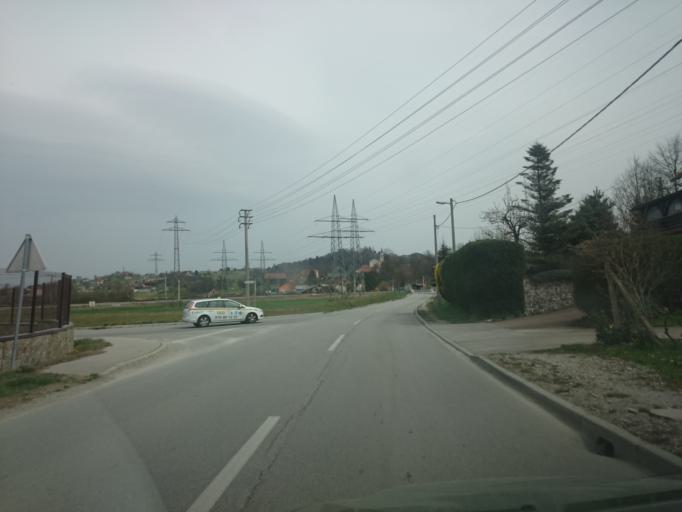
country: SI
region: Store
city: Store
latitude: 46.2301
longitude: 15.2936
